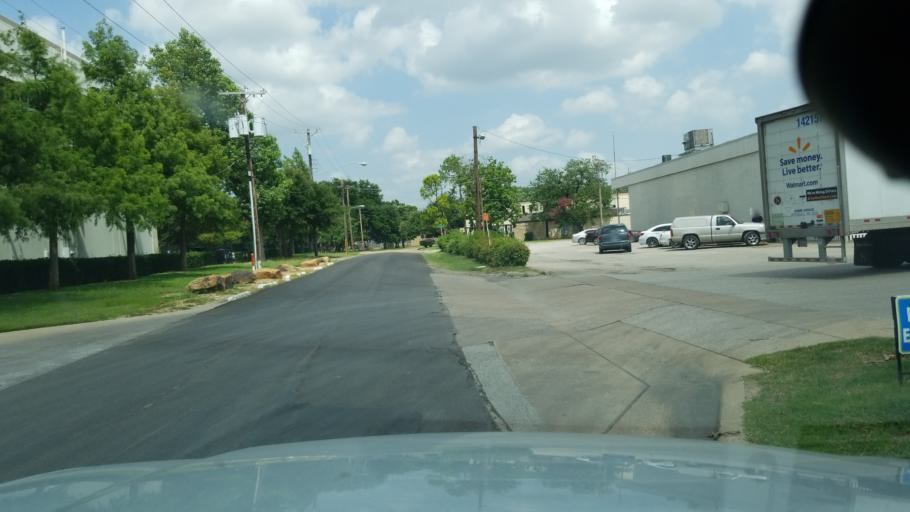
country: US
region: Texas
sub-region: Dallas County
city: University Park
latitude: 32.8297
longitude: -96.8610
